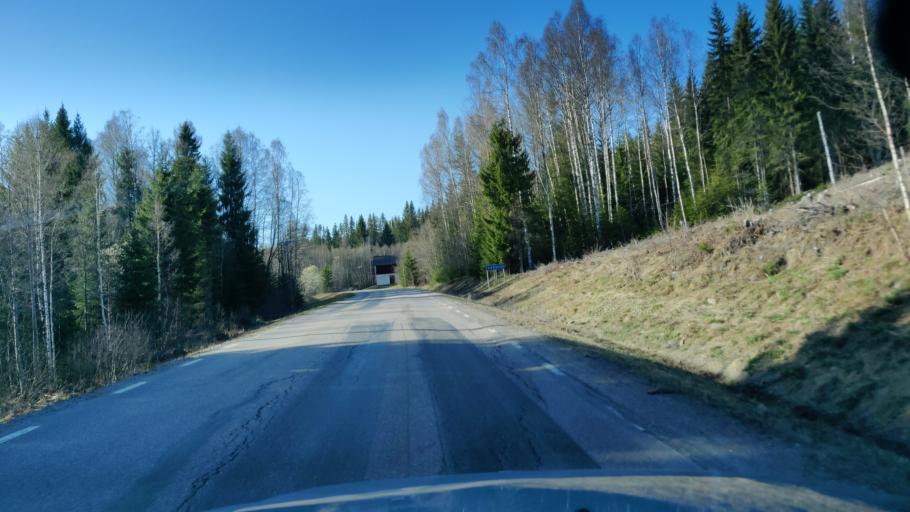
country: SE
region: Vaermland
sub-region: Munkfors Kommun
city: Munkfors
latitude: 59.9824
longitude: 13.4038
